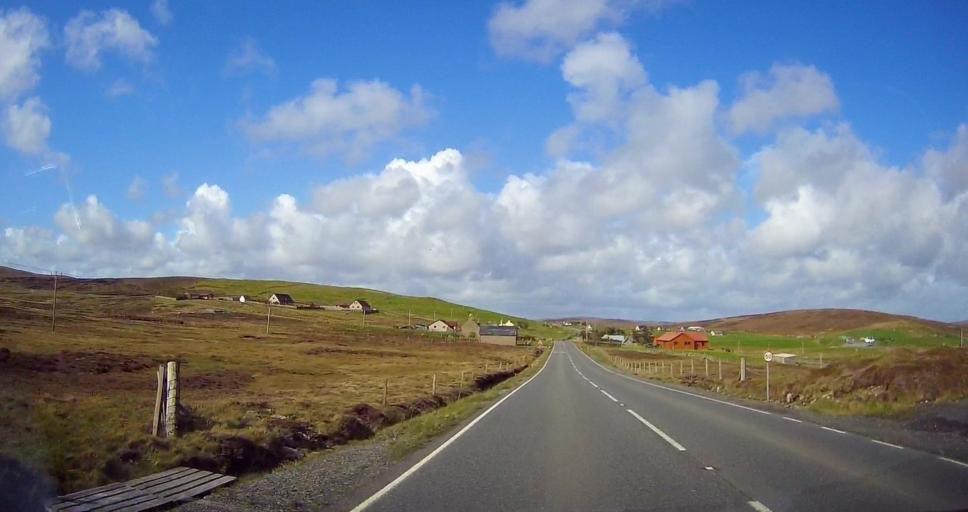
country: GB
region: Scotland
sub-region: Shetland Islands
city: Lerwick
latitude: 60.2329
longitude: -1.2353
